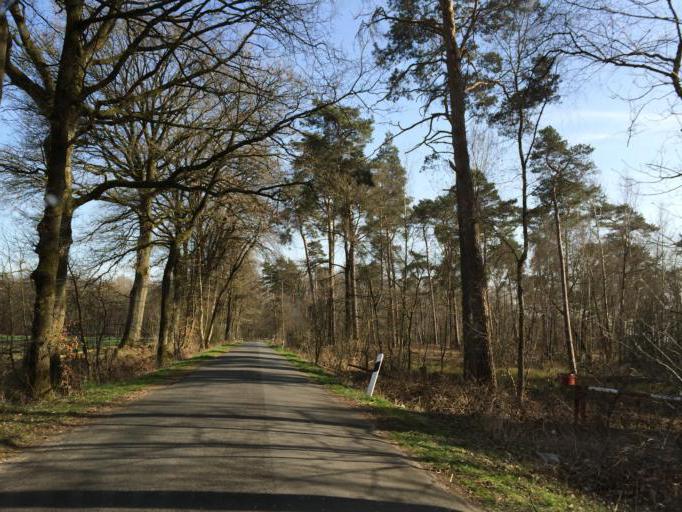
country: DE
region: North Rhine-Westphalia
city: Dorsten
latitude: 51.7047
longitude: 7.0273
